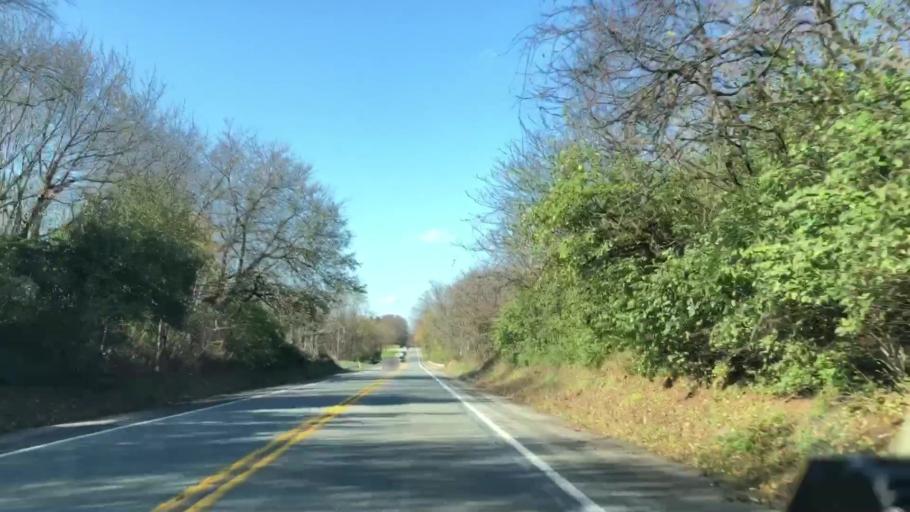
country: US
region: Pennsylvania
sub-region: Montgomery County
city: Sanatoga
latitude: 40.2159
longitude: -75.6045
